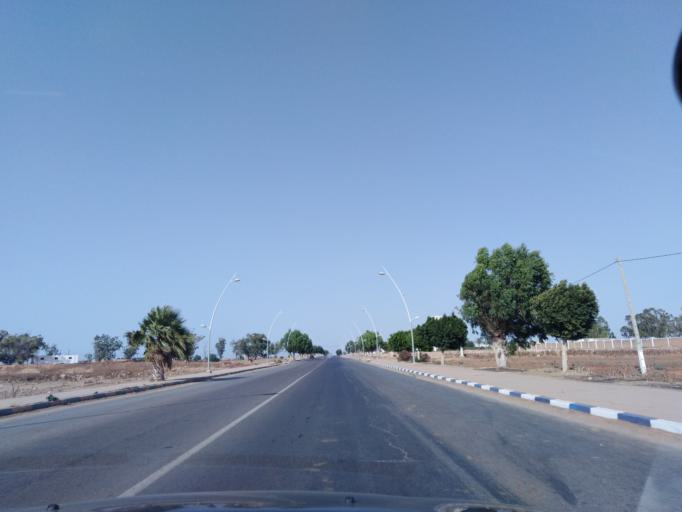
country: MA
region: Doukkala-Abda
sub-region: Safi
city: Safi
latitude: 32.2563
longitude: -8.9769
